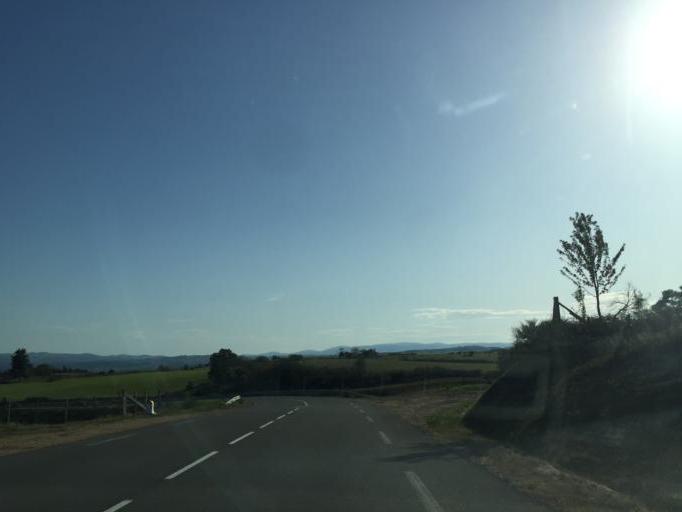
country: FR
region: Rhone-Alpes
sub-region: Departement de la Loire
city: Perigneux
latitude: 45.4662
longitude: 4.1270
